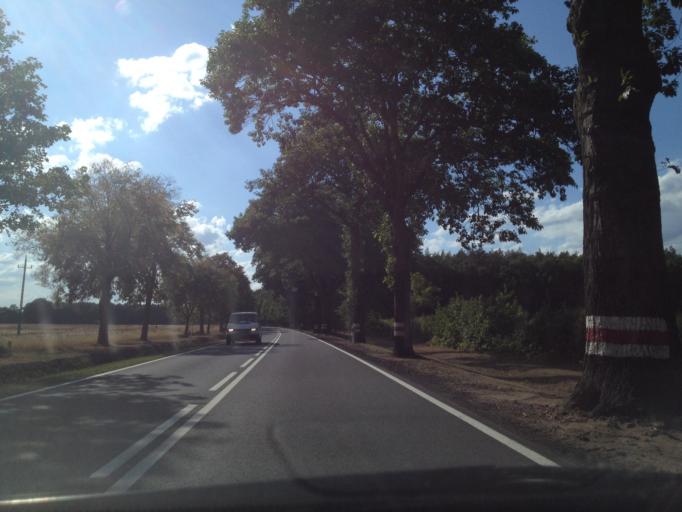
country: PL
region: Lubusz
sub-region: Powiat zarski
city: Lipinki Luzyckie
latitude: 51.6371
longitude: 14.9169
